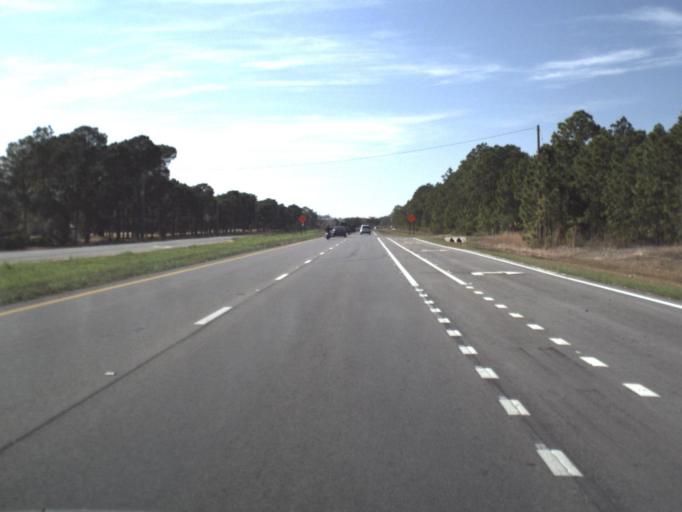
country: US
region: Florida
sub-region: Bay County
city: Panama City Beach
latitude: 30.1931
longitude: -85.8013
